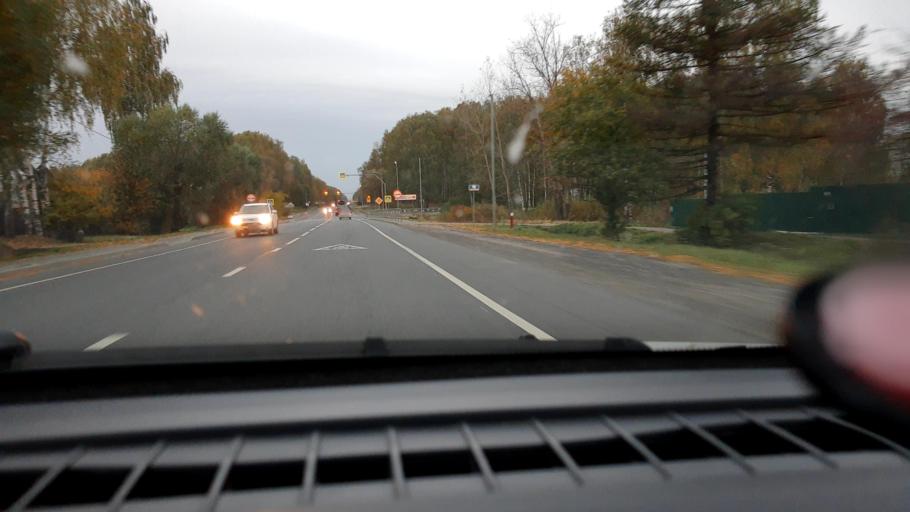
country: RU
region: Vladimir
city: Orgtrud
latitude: 56.2099
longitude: 40.6588
